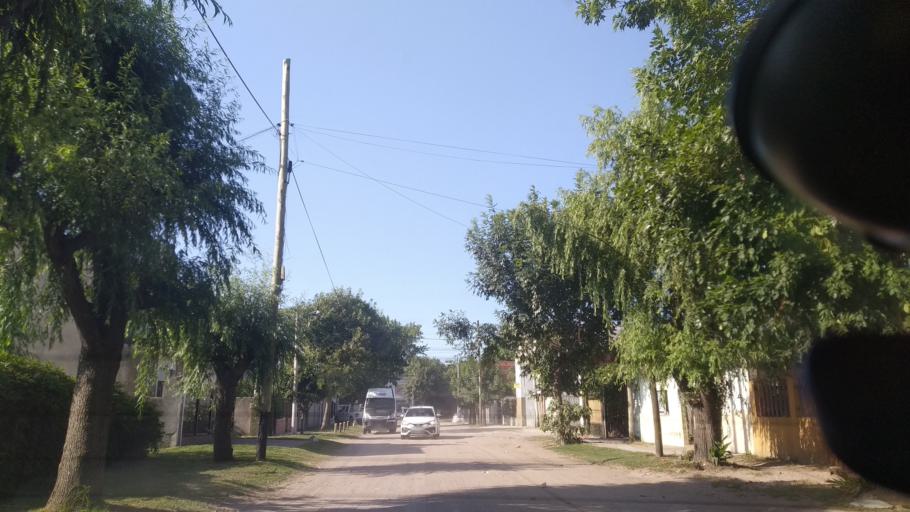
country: AR
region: Buenos Aires
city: Mar del Tuyu
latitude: -36.5343
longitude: -56.7117
